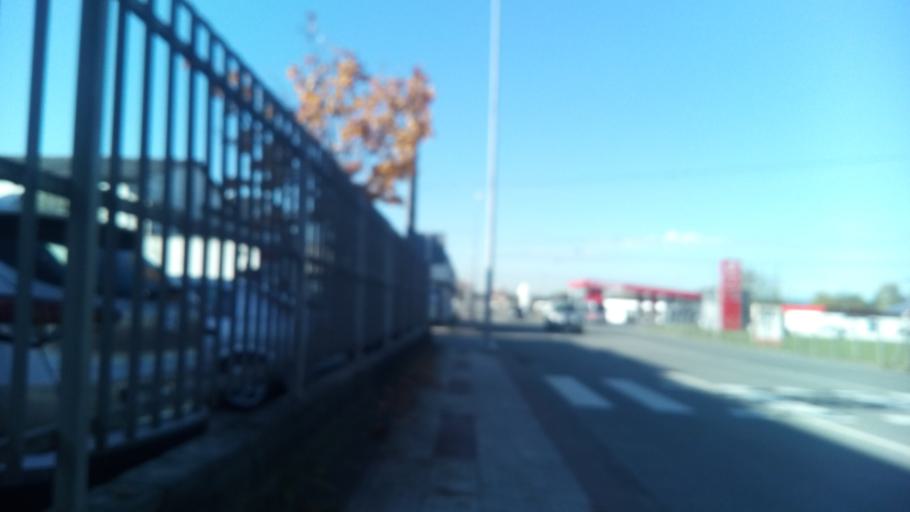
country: ES
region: Basque Country
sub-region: Bizkaia
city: Zamudio
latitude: 43.2793
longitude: -2.8518
